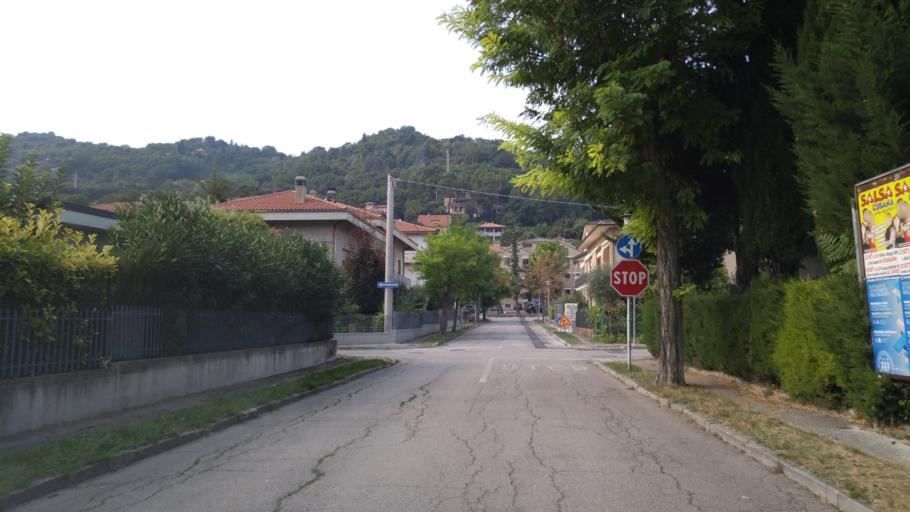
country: IT
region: The Marches
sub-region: Provincia di Pesaro e Urbino
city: Fossombrone
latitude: 43.6923
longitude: 12.8166
